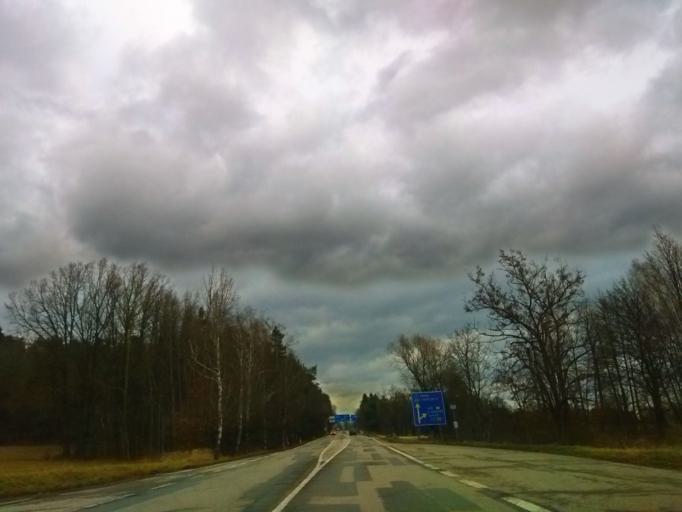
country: CZ
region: Jihocesky
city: Kamenny Ujezd
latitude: 48.8852
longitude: 14.4322
